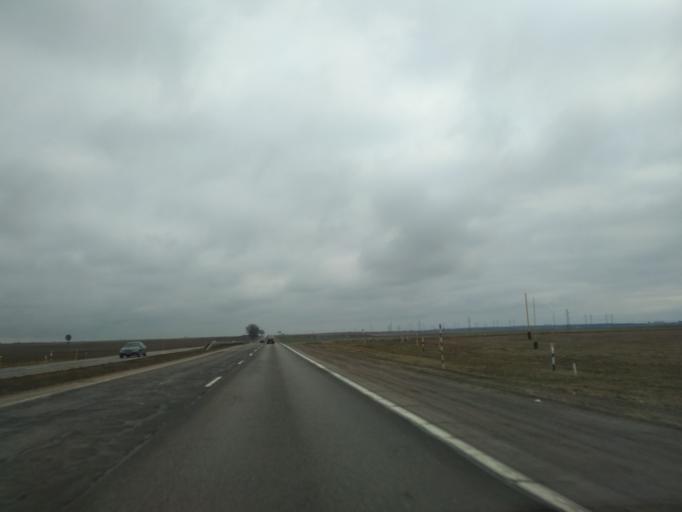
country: BY
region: Minsk
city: Dukora
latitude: 53.6943
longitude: 27.8969
